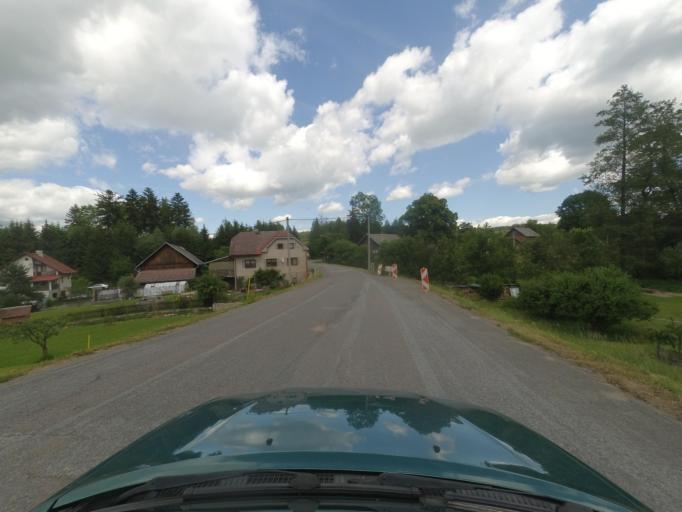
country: CZ
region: Pardubicky
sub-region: Okres Usti nad Orlici
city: Kunvald
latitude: 50.0966
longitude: 16.5162
